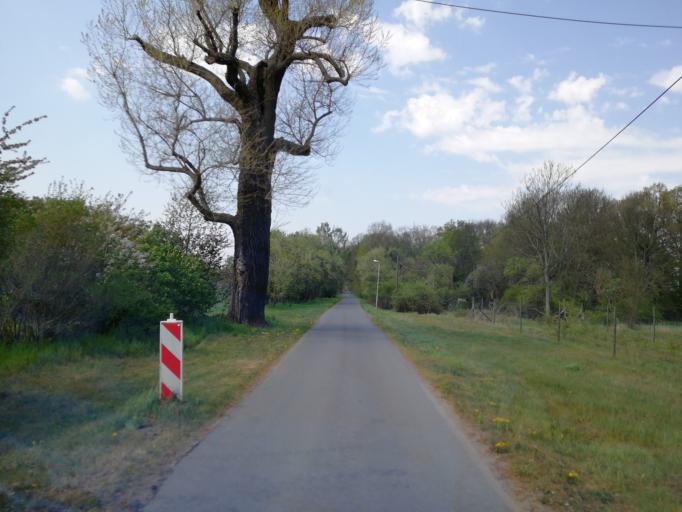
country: DE
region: Brandenburg
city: Bronkow
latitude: 51.7360
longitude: 13.8601
